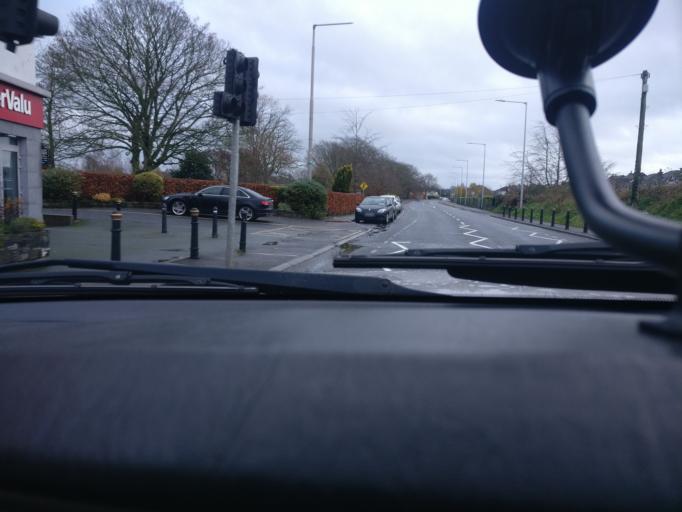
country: IE
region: Leinster
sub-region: An Mhi
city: Enfield
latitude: 53.4140
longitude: -6.8274
